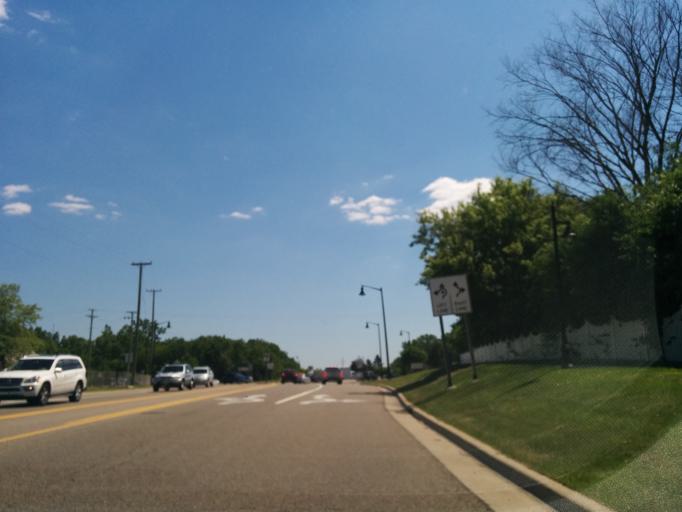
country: US
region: Michigan
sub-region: Oakland County
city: West Bloomfield Township
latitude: 42.5294
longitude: -83.3798
